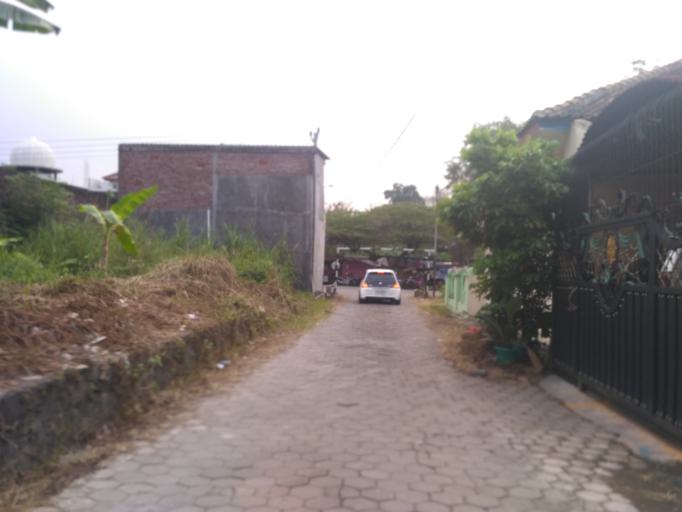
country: ID
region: Central Java
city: Mranggen
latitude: -7.0404
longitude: 110.4683
